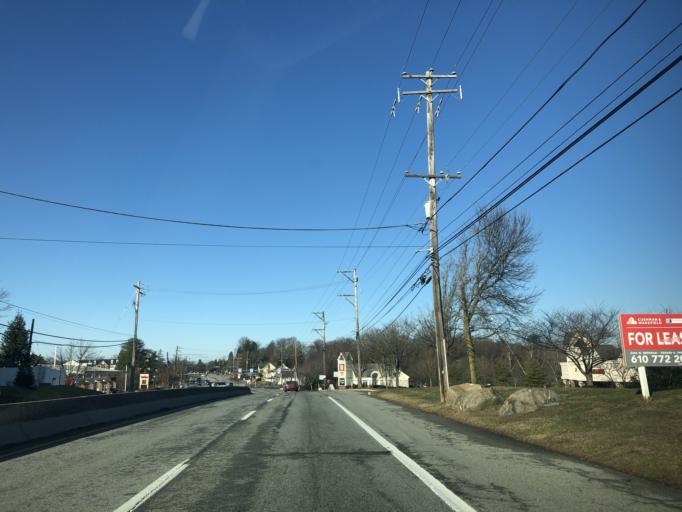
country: US
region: Pennsylvania
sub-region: Delaware County
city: Chester Heights
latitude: 39.8968
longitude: -75.4838
